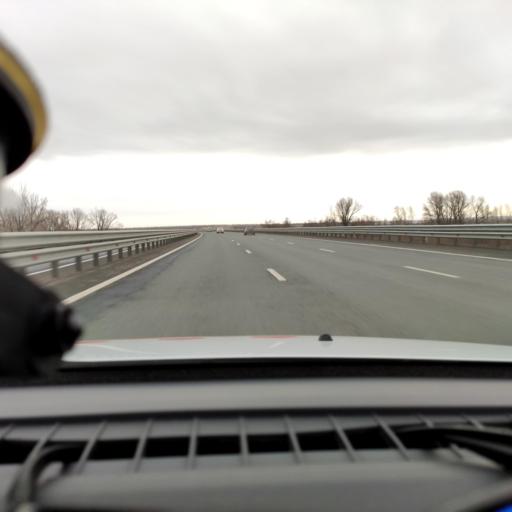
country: RU
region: Samara
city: Smyshlyayevka
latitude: 53.1684
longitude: 50.3166
